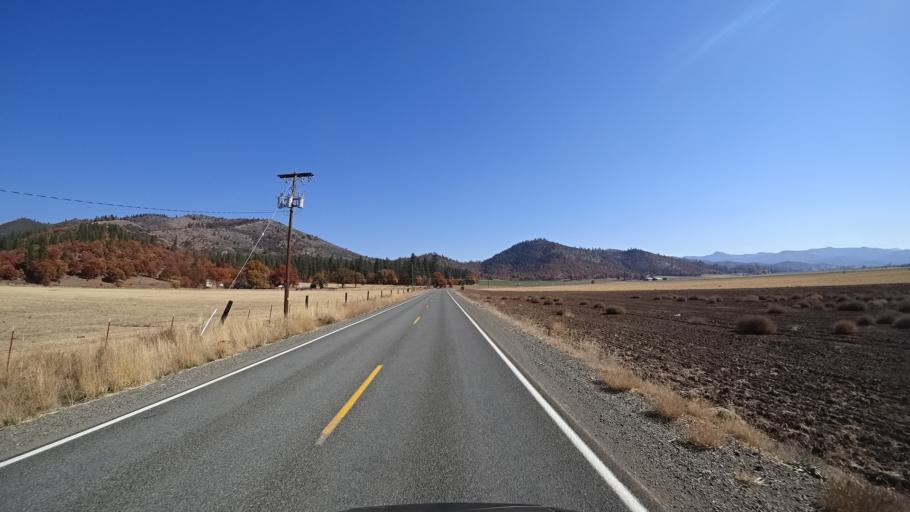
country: US
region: California
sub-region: Siskiyou County
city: Yreka
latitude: 41.6285
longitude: -122.8767
